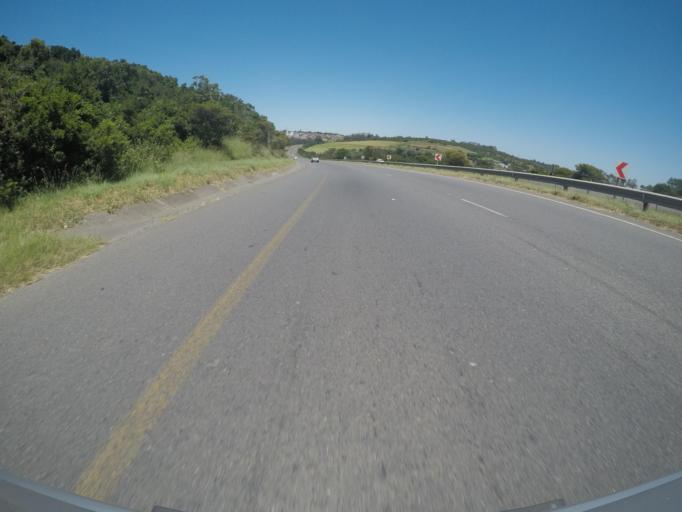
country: ZA
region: Eastern Cape
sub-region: Buffalo City Metropolitan Municipality
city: East London
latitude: -32.9420
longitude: 27.9439
